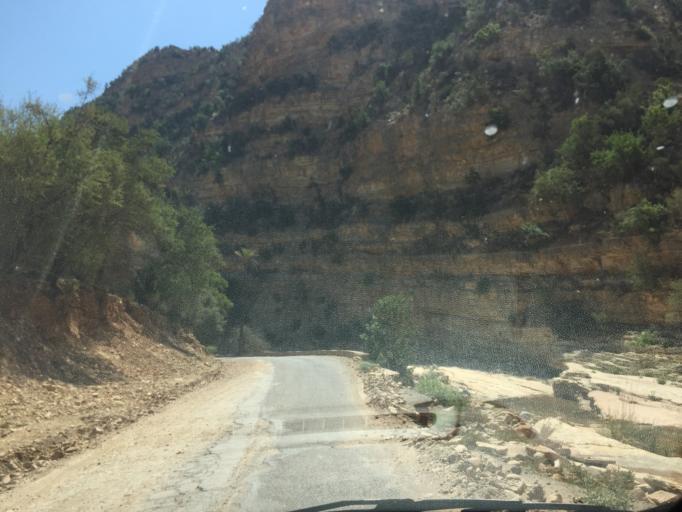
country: MA
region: Souss-Massa-Draa
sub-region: Agadir-Ida-ou-Tnan
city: Aourir
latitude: 30.5641
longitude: -9.5409
